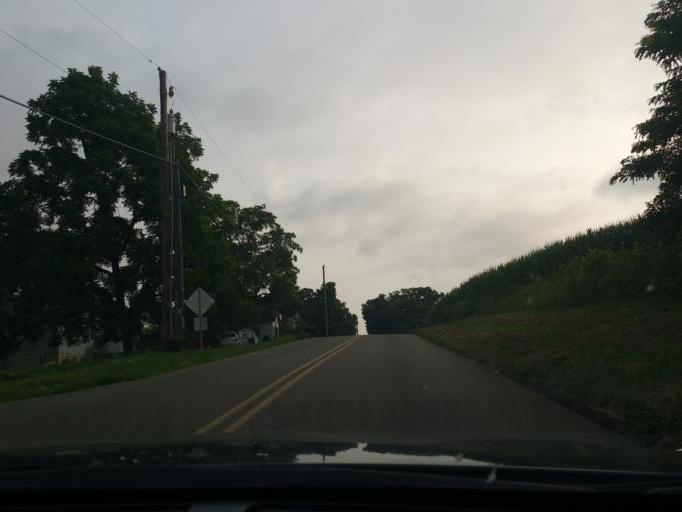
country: US
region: Maryland
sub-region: Cecil County
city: Rising Sun
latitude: 39.7280
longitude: -76.1957
